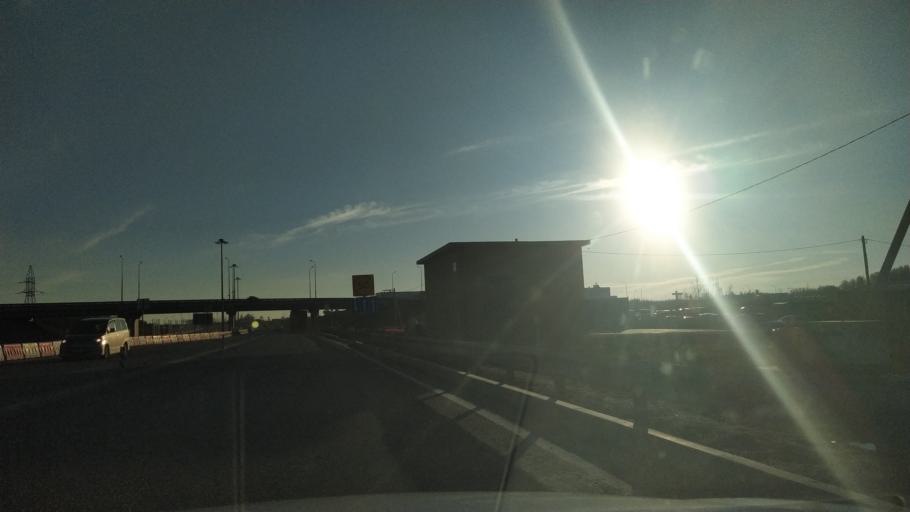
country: RU
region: St.-Petersburg
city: Pargolovo
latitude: 60.0989
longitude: 30.2710
